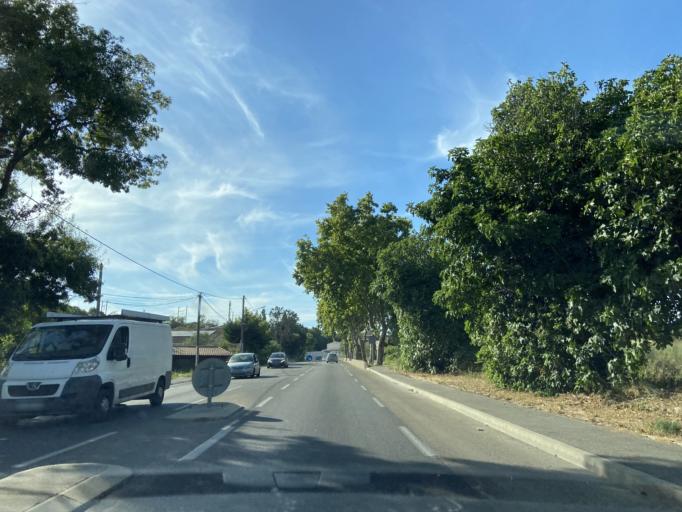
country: FR
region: Provence-Alpes-Cote d'Azur
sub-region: Departement des Bouches-du-Rhone
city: Miramas
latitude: 43.5753
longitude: 5.0162
